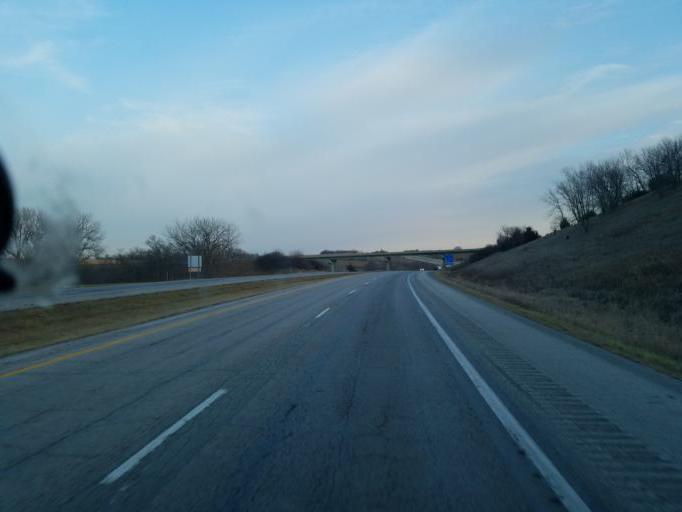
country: US
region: Iowa
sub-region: Harrison County
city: Missouri Valley
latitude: 41.4946
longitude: -95.8639
